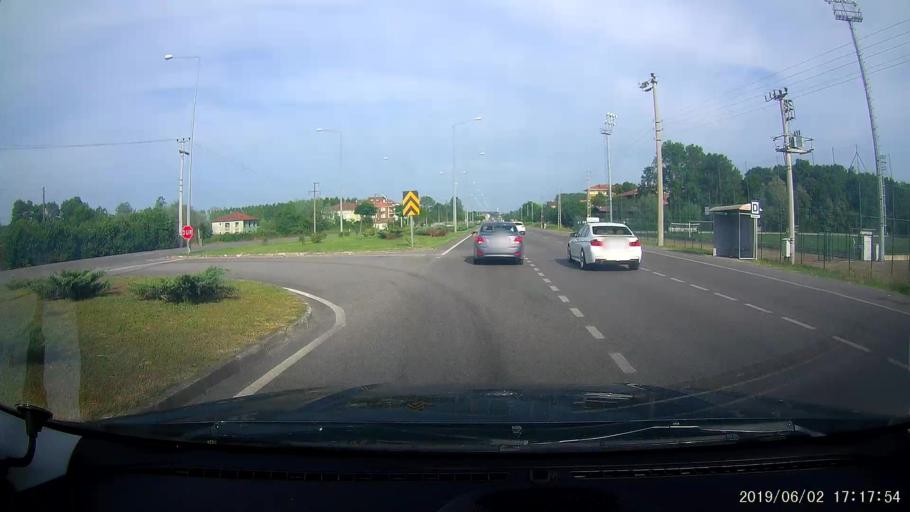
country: TR
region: Samsun
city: Dikbiyik
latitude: 41.2263
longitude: 36.5891
